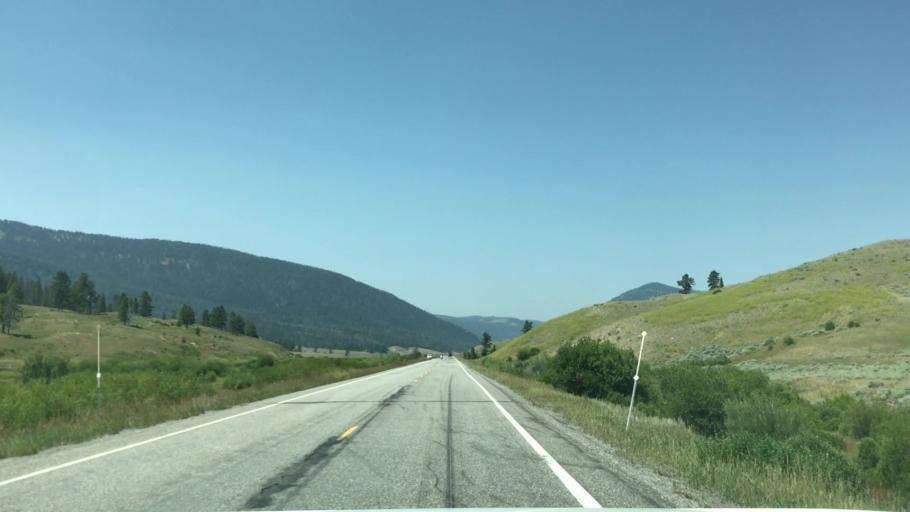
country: US
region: Montana
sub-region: Gallatin County
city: Big Sky
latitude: 45.0395
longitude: -111.1214
